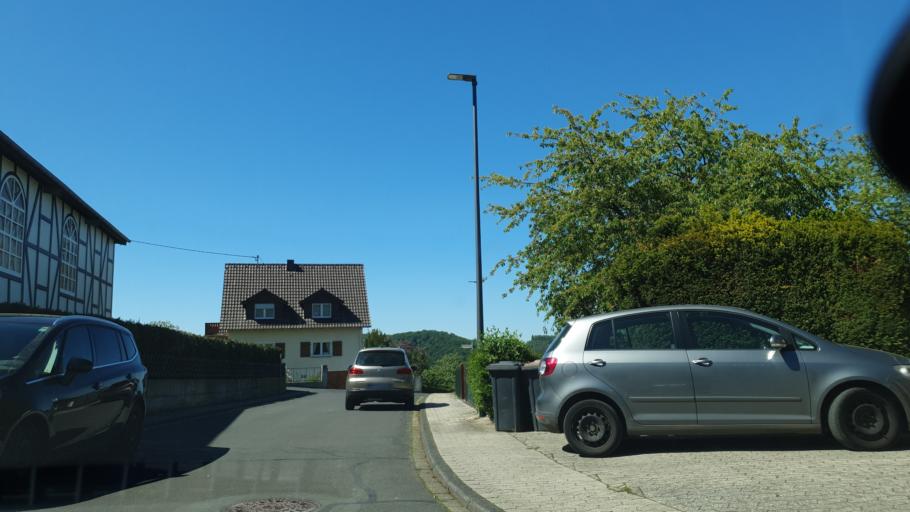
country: DE
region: Rheinland-Pfalz
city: Frucht
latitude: 50.3139
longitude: 7.6784
